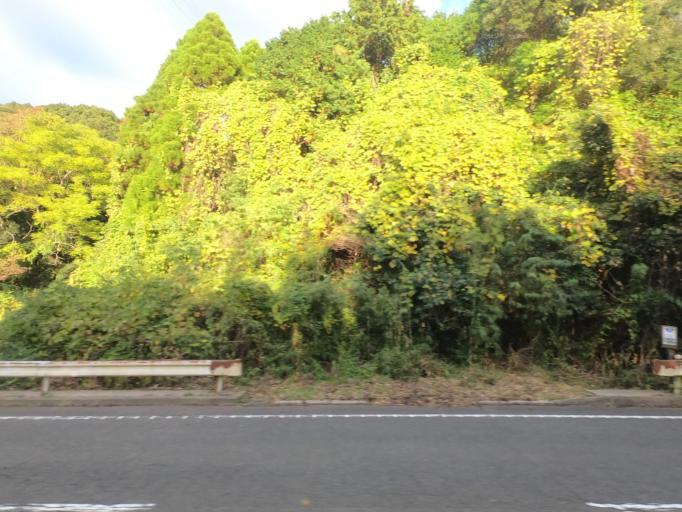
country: JP
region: Kumamoto
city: Minamata
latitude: 32.2435
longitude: 130.4795
